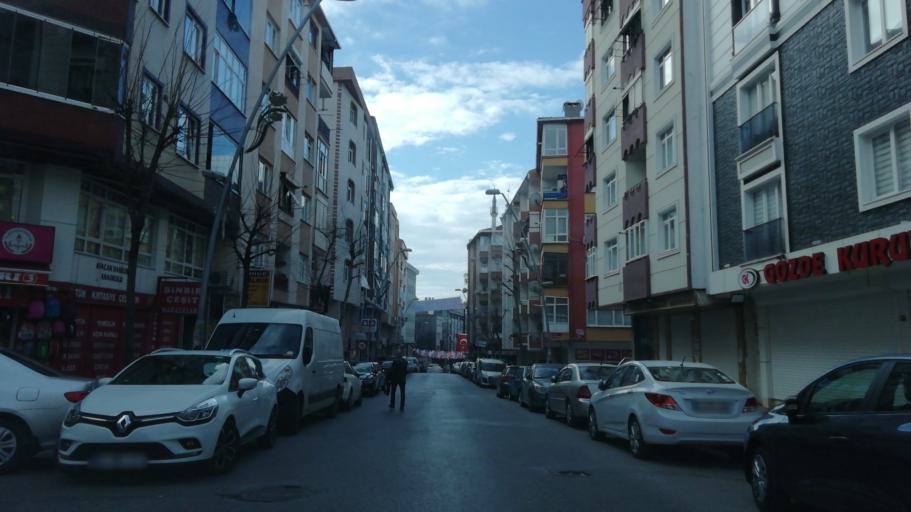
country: TR
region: Istanbul
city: Bahcelievler
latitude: 40.9956
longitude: 28.8411
